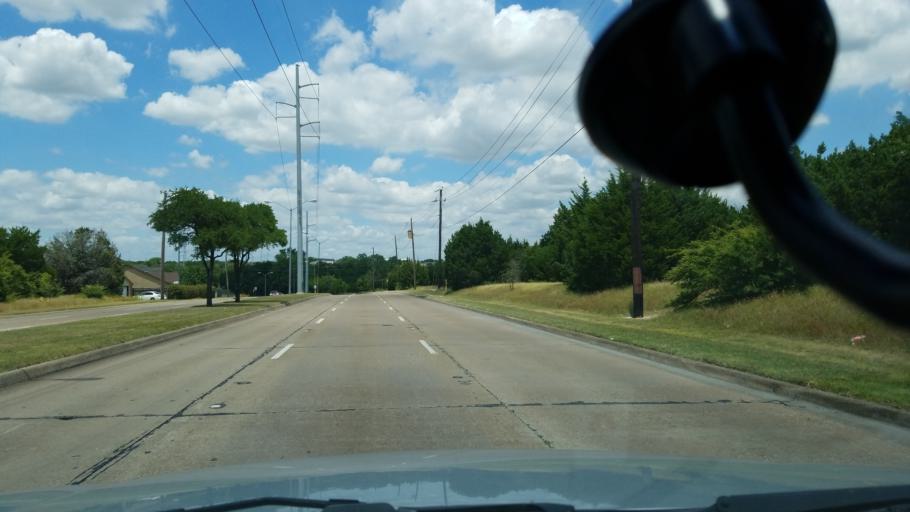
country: US
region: Texas
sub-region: Dallas County
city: Duncanville
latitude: 32.6687
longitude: -96.8816
